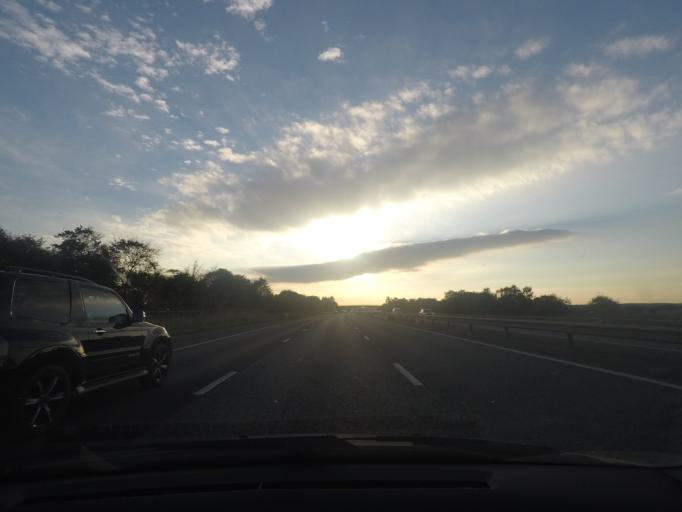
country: GB
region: England
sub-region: North Lincolnshire
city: Brigg
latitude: 53.5639
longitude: -0.4853
